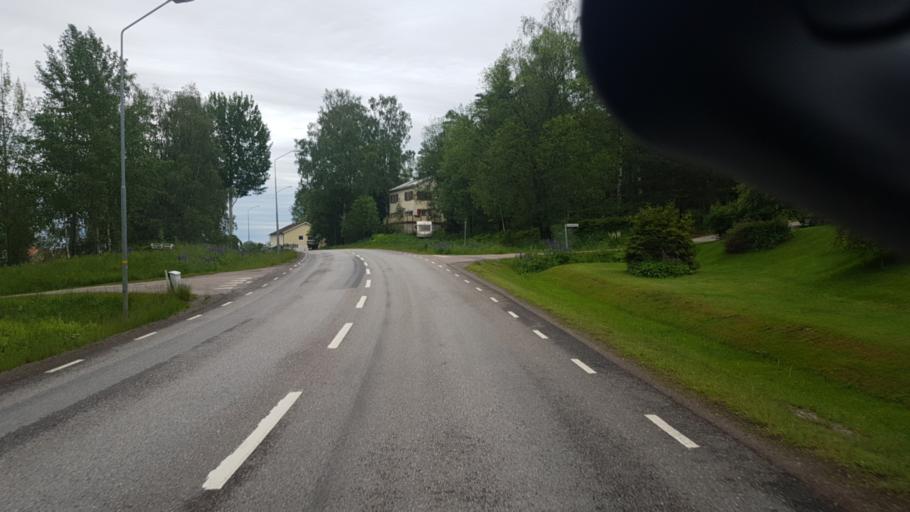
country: SE
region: Vaermland
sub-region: Eda Kommun
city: Amotfors
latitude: 59.7141
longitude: 12.1593
